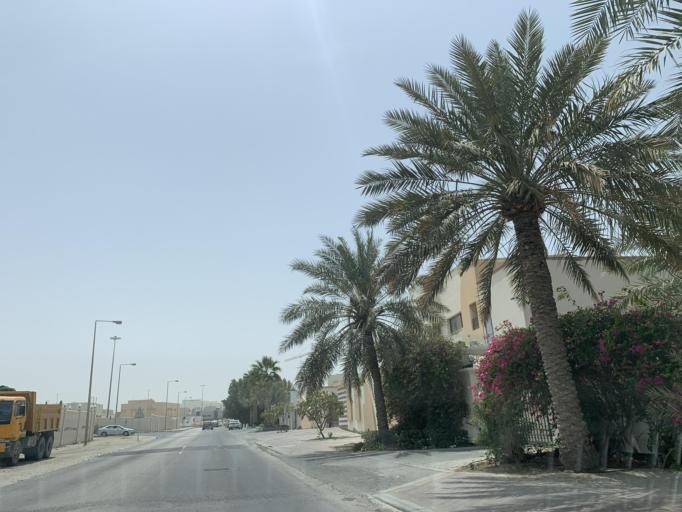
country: BH
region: Northern
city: Madinat `Isa
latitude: 26.1613
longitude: 50.5277
